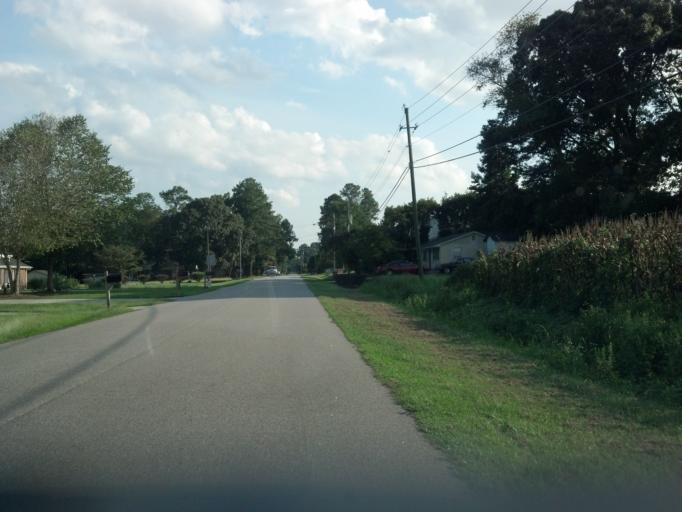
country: US
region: North Carolina
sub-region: Pitt County
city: Ayden
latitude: 35.4746
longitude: -77.4090
